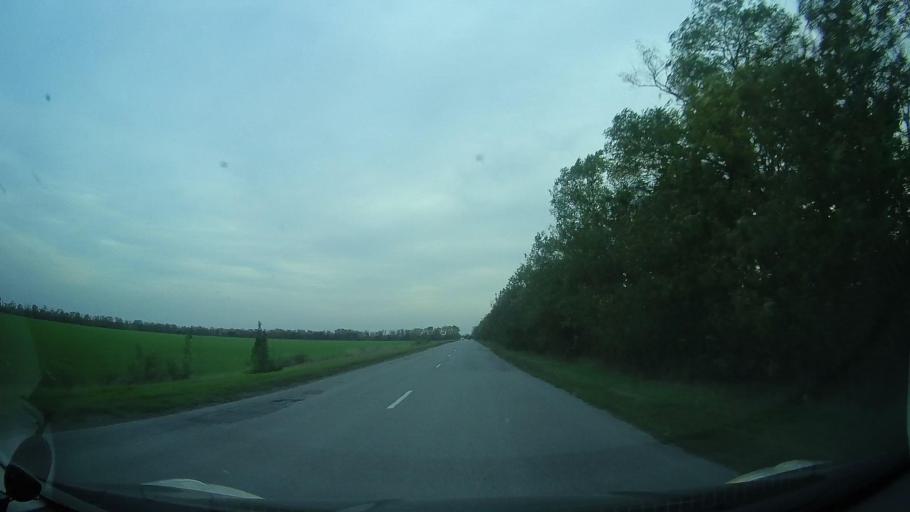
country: RU
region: Rostov
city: Kirovskaya
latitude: 47.0066
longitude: 39.9789
